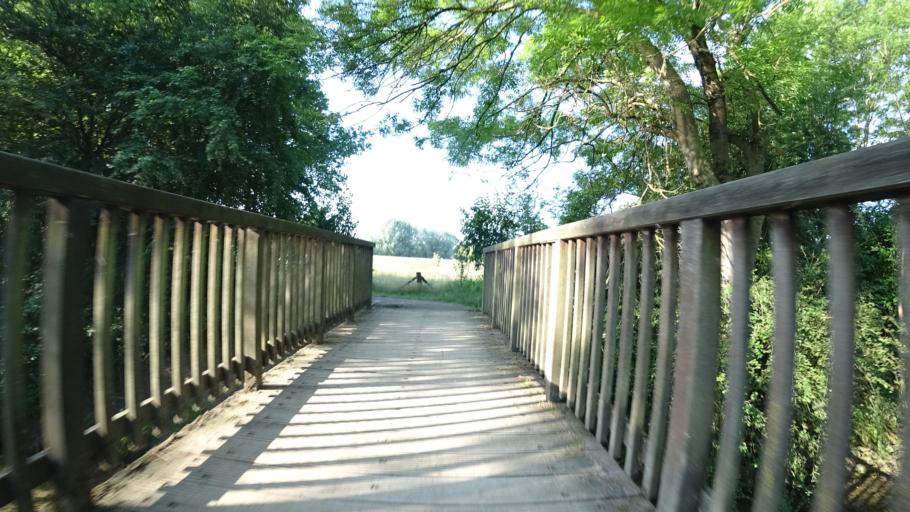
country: DE
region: North Rhine-Westphalia
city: Erwitte
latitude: 51.6380
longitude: 8.3735
